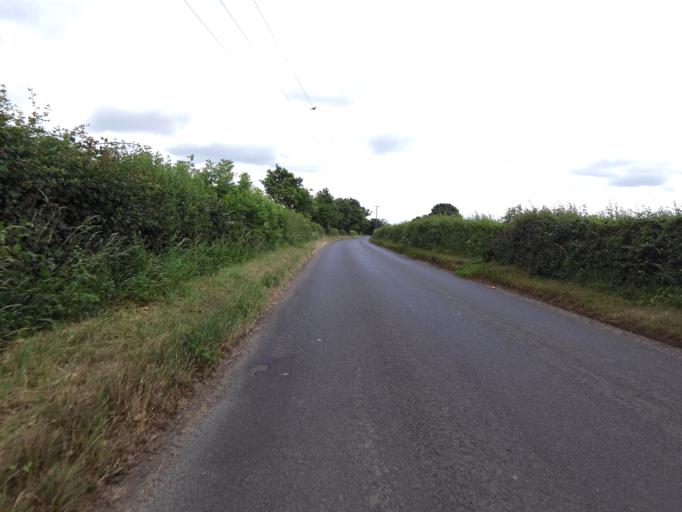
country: GB
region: England
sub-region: Norfolk
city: Harleston
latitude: 52.4026
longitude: 1.2857
